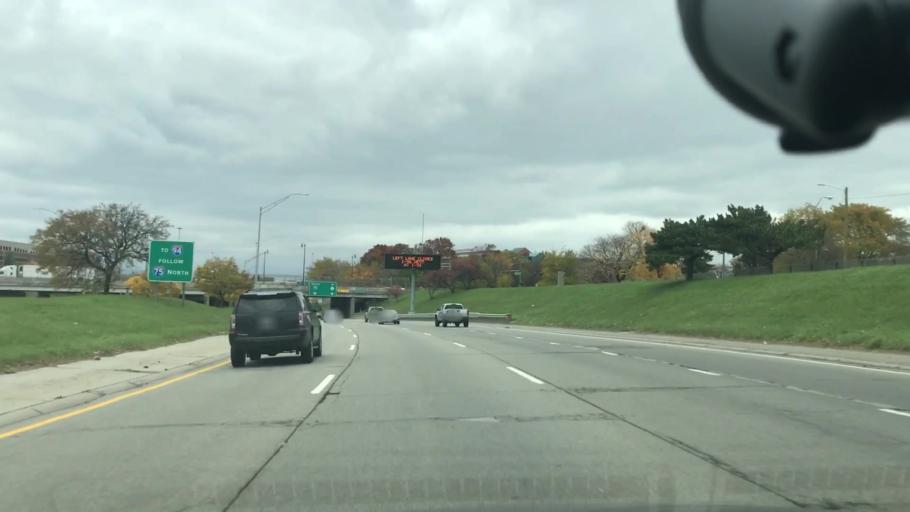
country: US
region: Michigan
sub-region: Wayne County
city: Detroit
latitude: 42.3387
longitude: -83.0397
